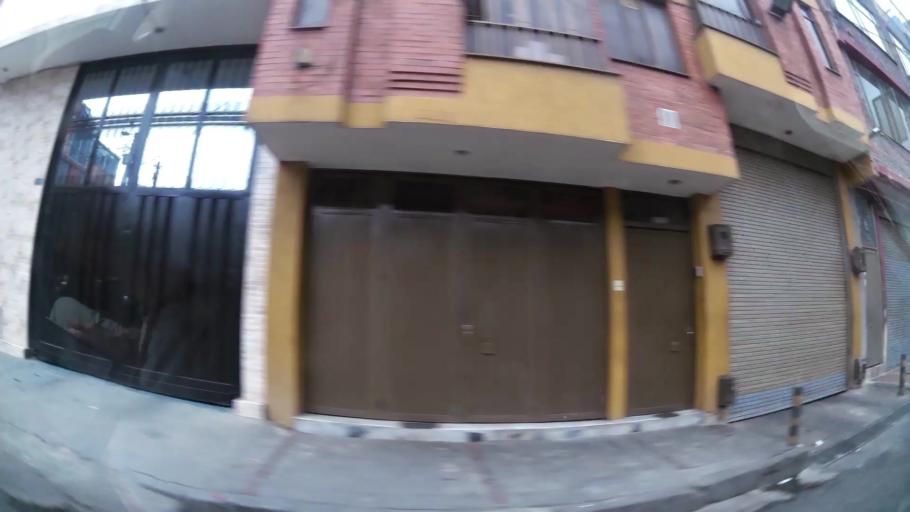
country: CO
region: Bogota D.C.
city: Barrio San Luis
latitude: 4.6992
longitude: -74.1073
